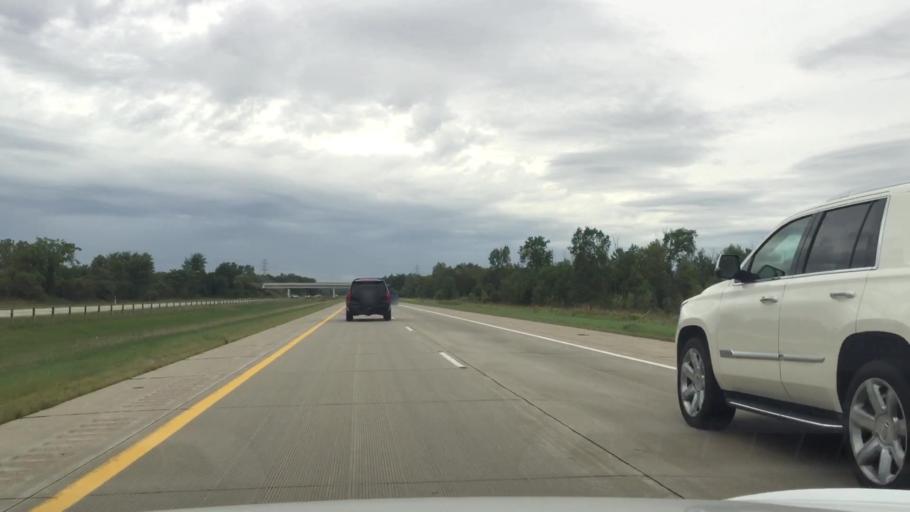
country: US
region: Michigan
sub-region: Macomb County
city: Richmond
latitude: 42.7548
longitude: -82.7052
